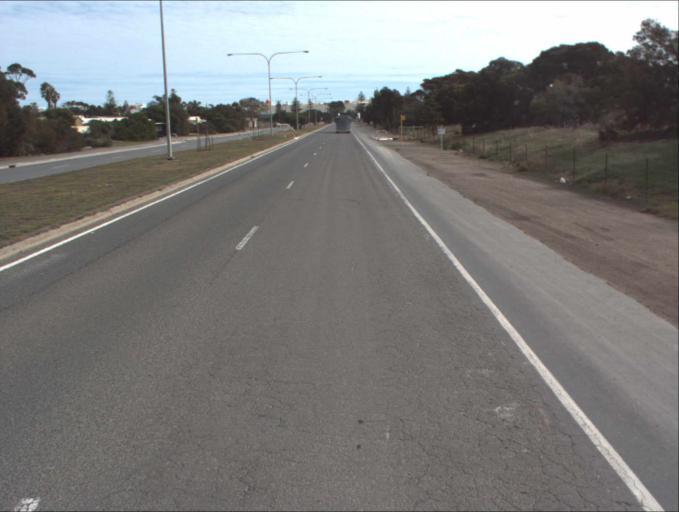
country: AU
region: South Australia
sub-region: Port Adelaide Enfield
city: Birkenhead
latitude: -34.7793
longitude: 138.4942
